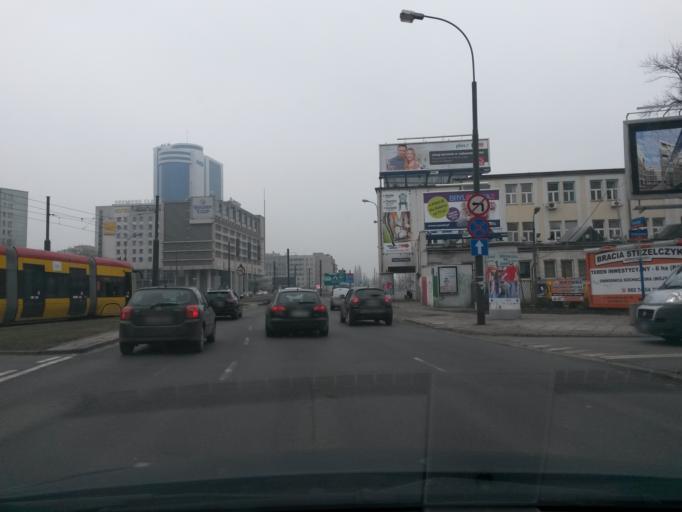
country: PL
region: Masovian Voivodeship
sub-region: Warszawa
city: Ochota
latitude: 52.2274
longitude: 20.9868
